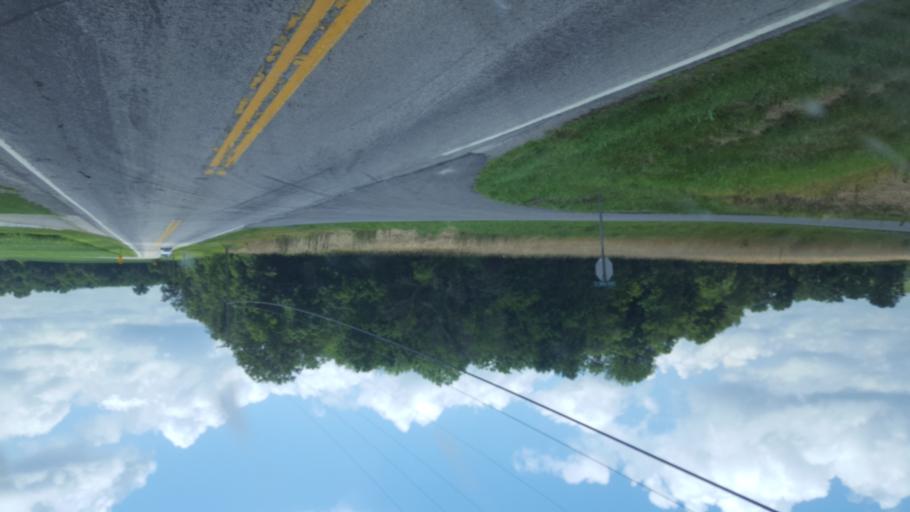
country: US
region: Ohio
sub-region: Highland County
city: Greenfield
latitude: 39.2439
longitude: -83.4364
